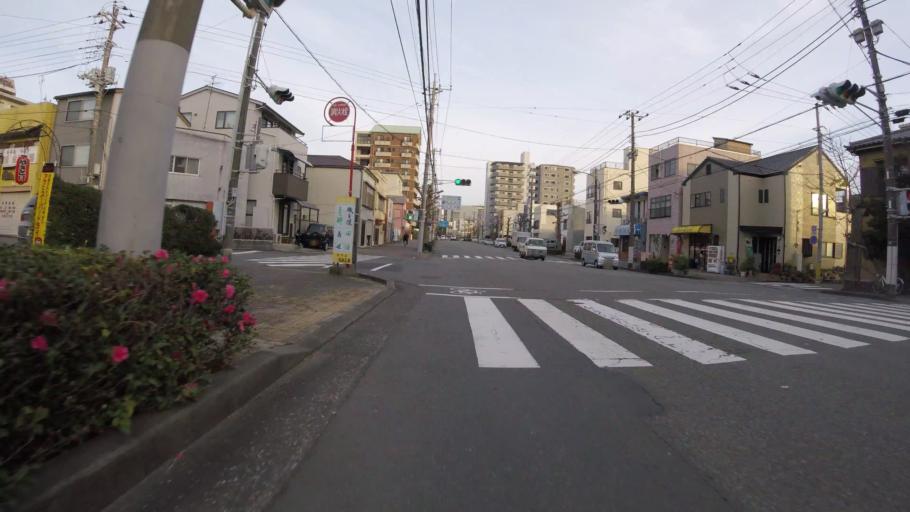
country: JP
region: Shizuoka
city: Numazu
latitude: 35.0973
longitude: 138.8528
